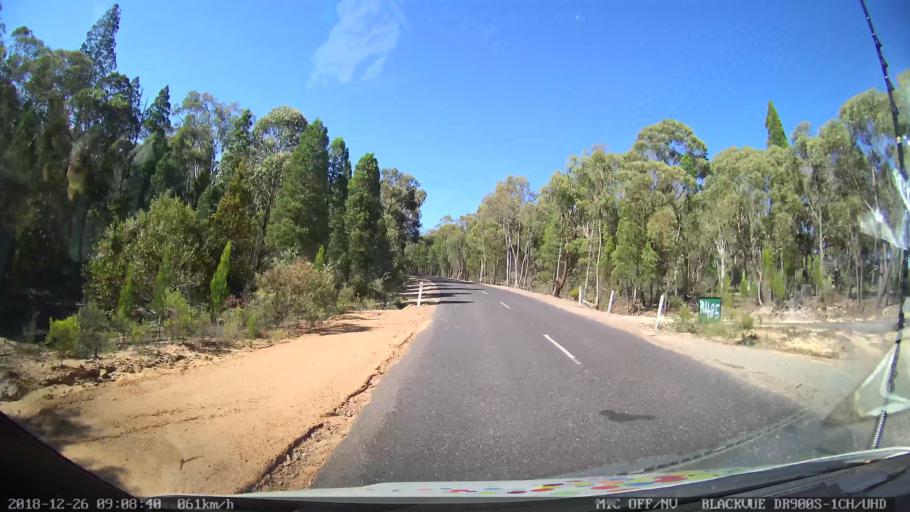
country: AU
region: New South Wales
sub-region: Mid-Western Regional
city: Kandos
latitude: -32.7175
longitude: 150.0005
